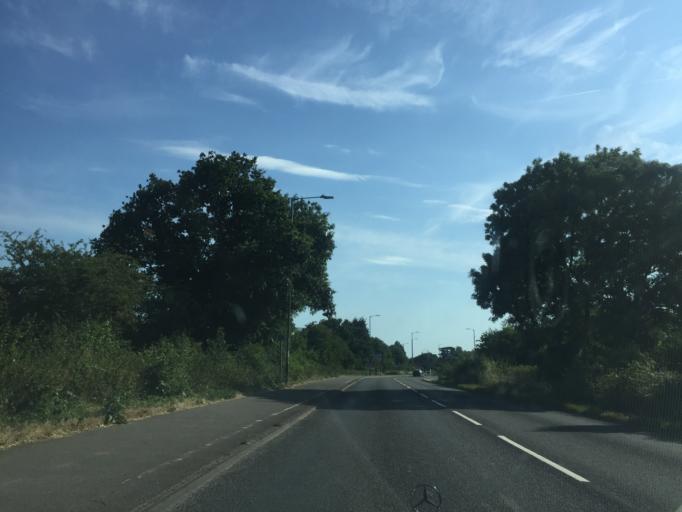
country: GB
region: England
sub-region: Warwickshire
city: Warwick
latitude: 52.2654
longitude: -1.6017
